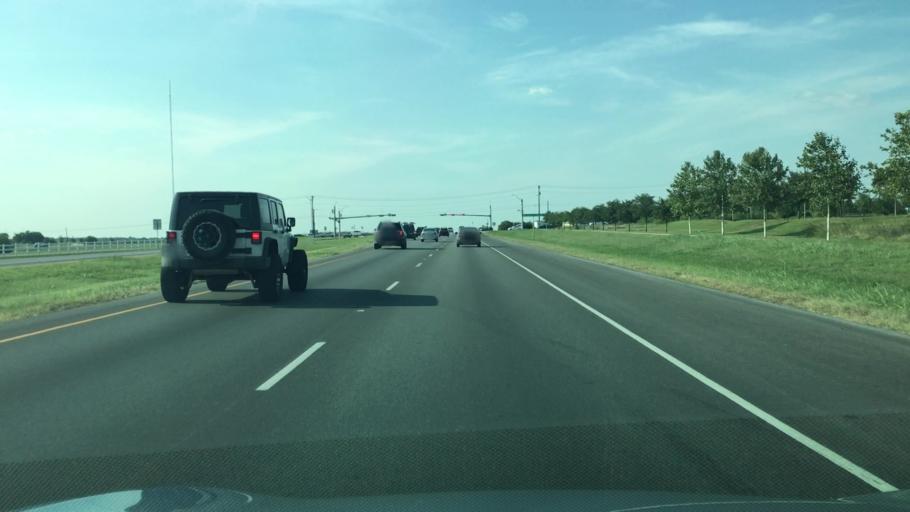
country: US
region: Texas
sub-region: Hays County
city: Kyle
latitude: 30.0256
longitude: -97.8723
